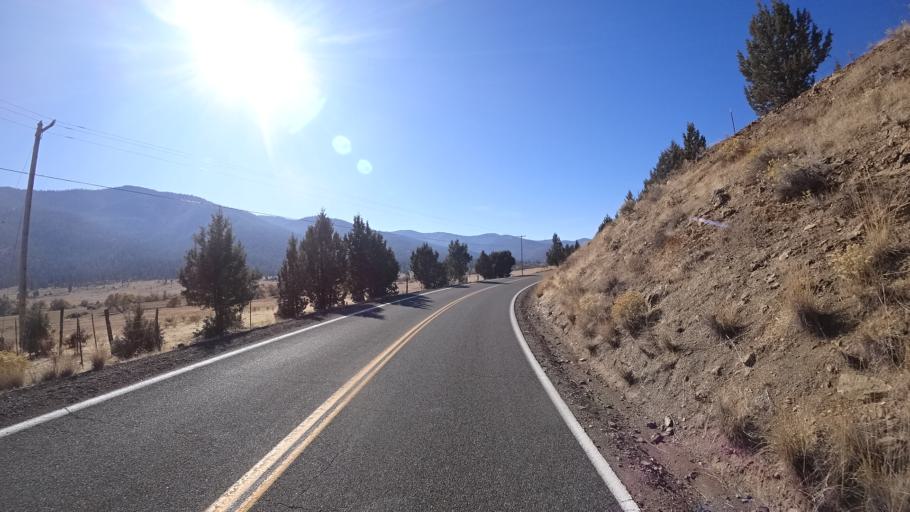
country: US
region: California
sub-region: Siskiyou County
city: Weed
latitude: 41.4938
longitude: -122.5548
